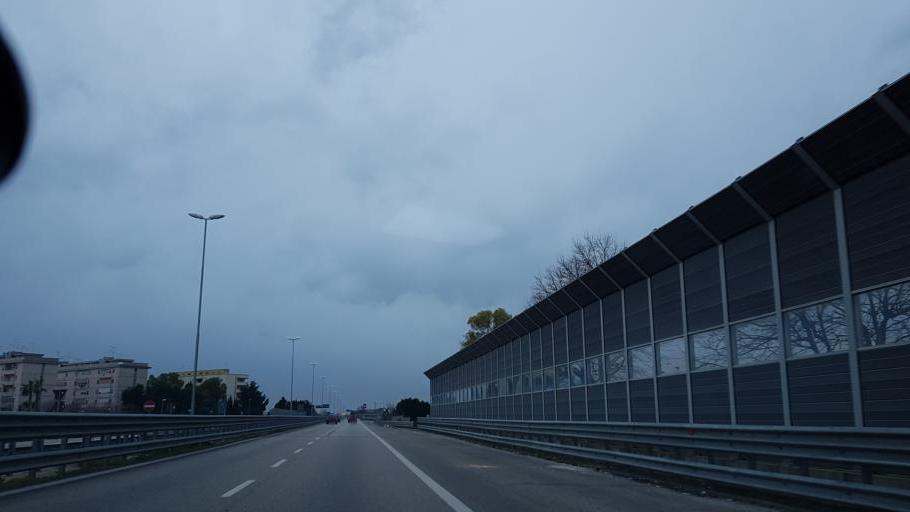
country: IT
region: Apulia
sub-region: Provincia di Brindisi
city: Brindisi
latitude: 40.6233
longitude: 17.9146
